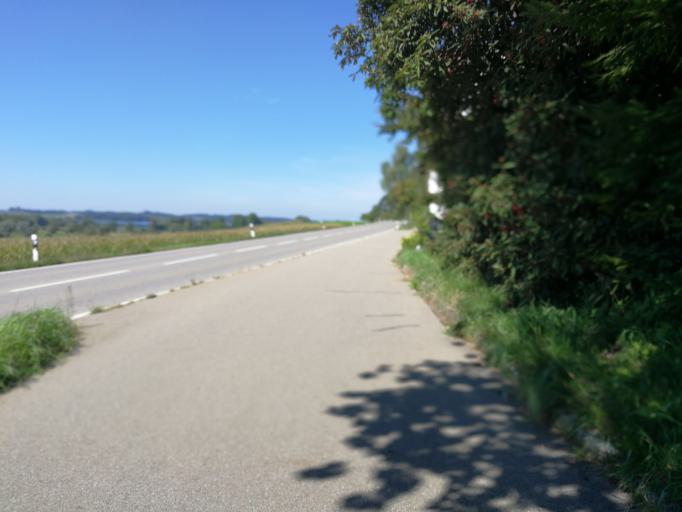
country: CH
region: Zurich
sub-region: Bezirk Hinwil
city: Wetzikon / Kempten
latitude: 47.3396
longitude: 8.8097
